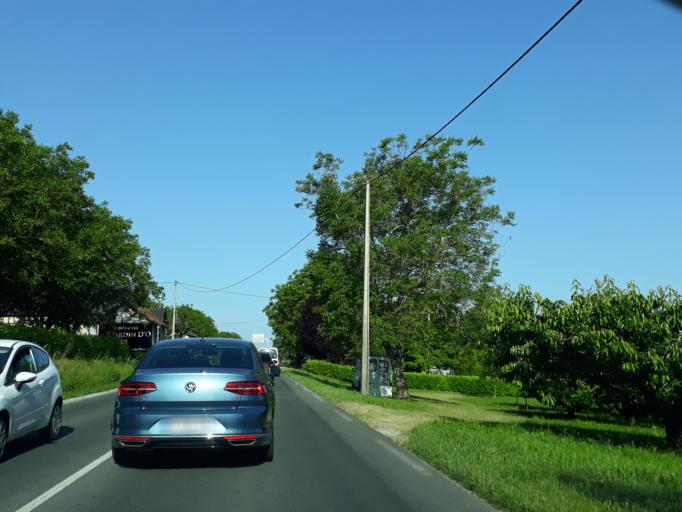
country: FR
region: Limousin
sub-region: Departement de la Correze
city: Cublac
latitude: 45.1280
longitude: 1.3342
